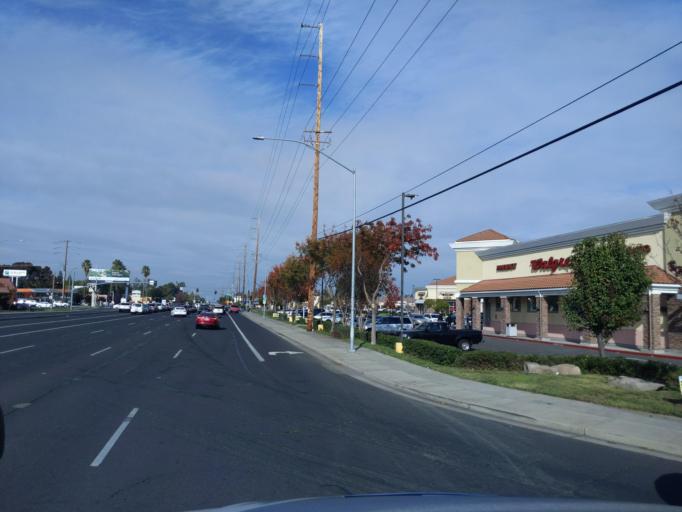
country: US
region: California
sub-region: San Joaquin County
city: Lincoln Village
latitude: 38.0193
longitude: -121.2947
